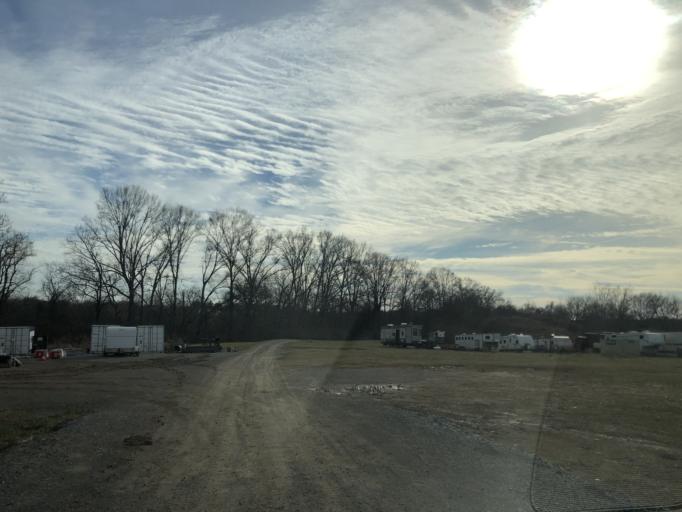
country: US
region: Tennessee
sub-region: Williamson County
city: Franklin
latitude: 35.9439
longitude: -86.8873
